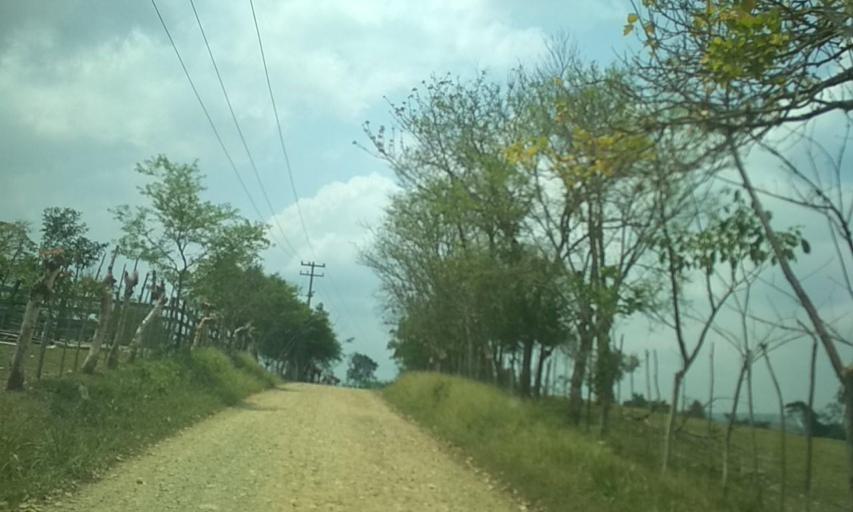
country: MX
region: Tabasco
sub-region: Huimanguillo
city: Francisco Rueda
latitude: 17.5914
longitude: -93.7938
